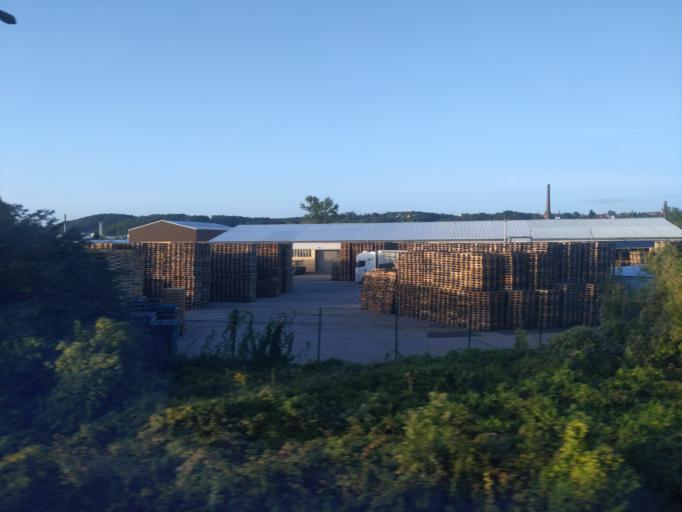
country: DE
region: Saxony
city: Niederau
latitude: 51.1618
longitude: 13.5169
